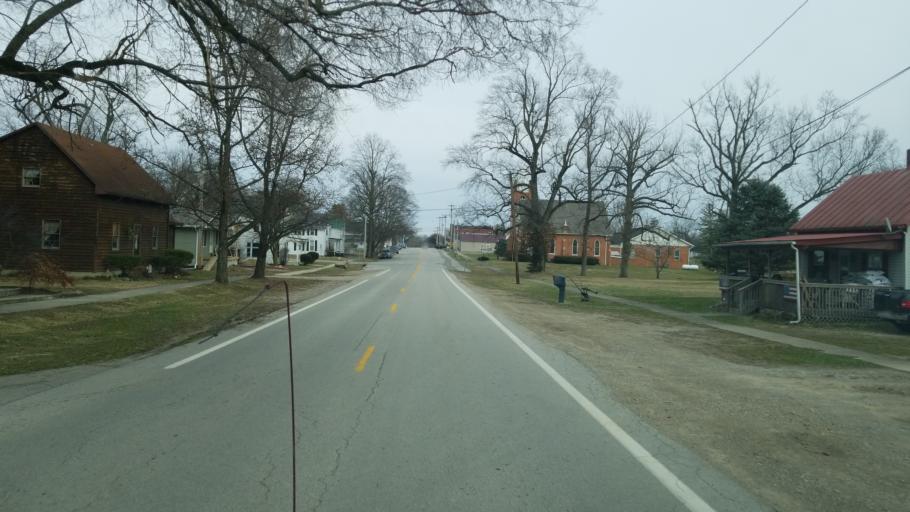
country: US
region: Ohio
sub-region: Pickaway County
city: Williamsport
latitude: 39.5046
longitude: -83.1570
